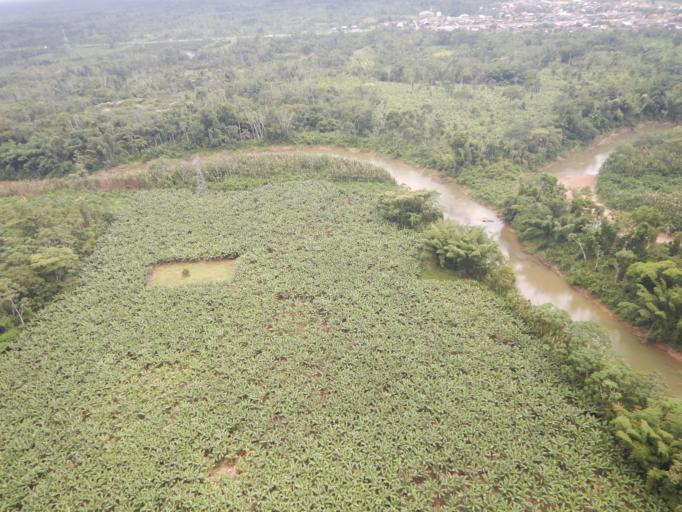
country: BO
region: Cochabamba
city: Chimore
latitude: -17.1507
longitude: -64.6882
